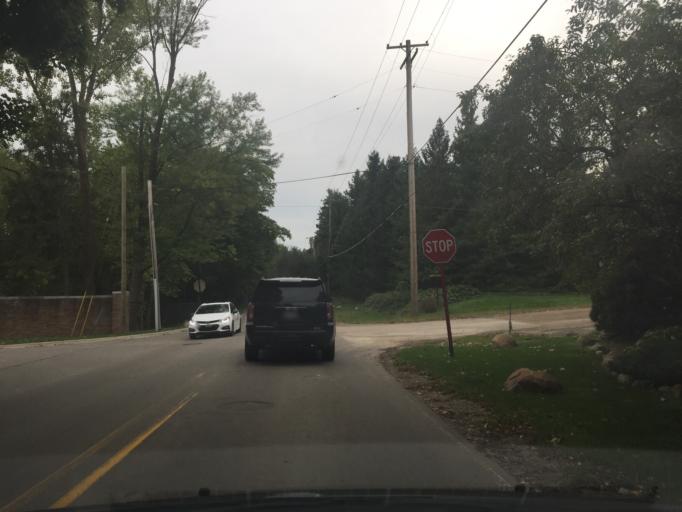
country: US
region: Michigan
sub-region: Oakland County
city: Bloomfield Hills
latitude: 42.5752
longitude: -83.2571
